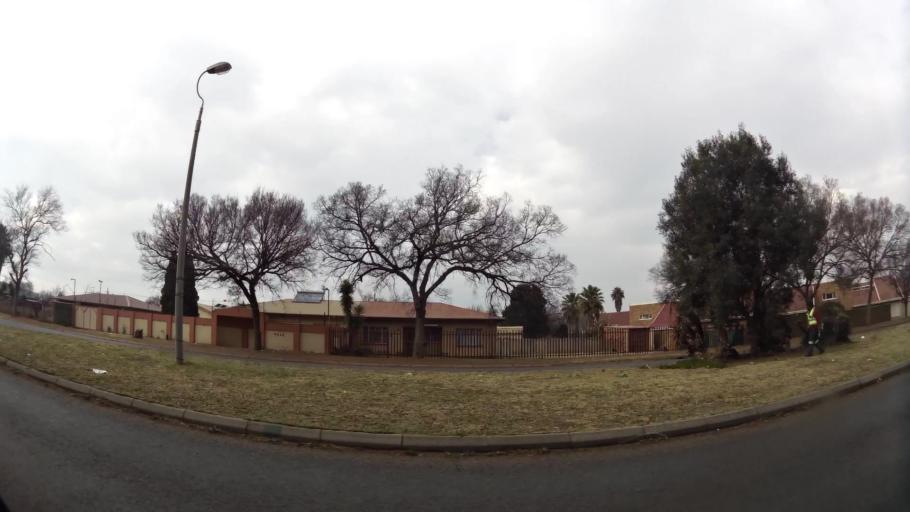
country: ZA
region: Gauteng
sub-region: Sedibeng District Municipality
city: Vanderbijlpark
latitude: -26.6877
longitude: 27.8263
